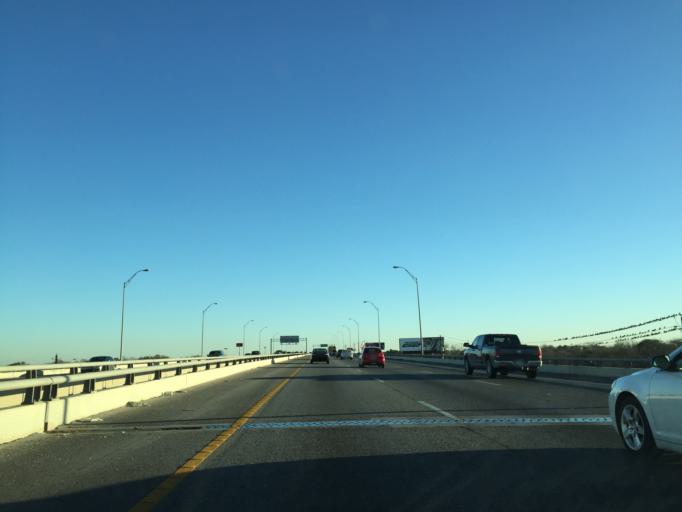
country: US
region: Texas
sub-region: Travis County
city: Wells Branch
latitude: 30.3640
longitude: -97.7178
